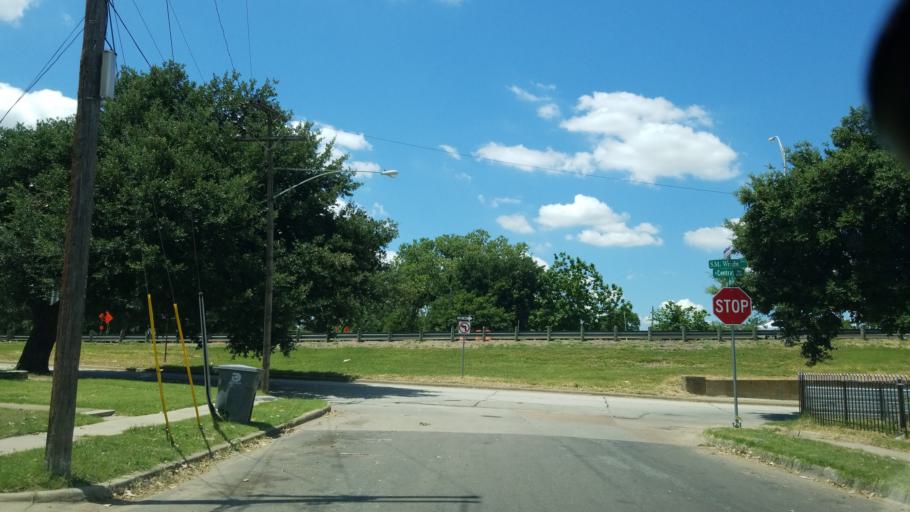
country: US
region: Texas
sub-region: Dallas County
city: Dallas
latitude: 32.7490
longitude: -96.7600
